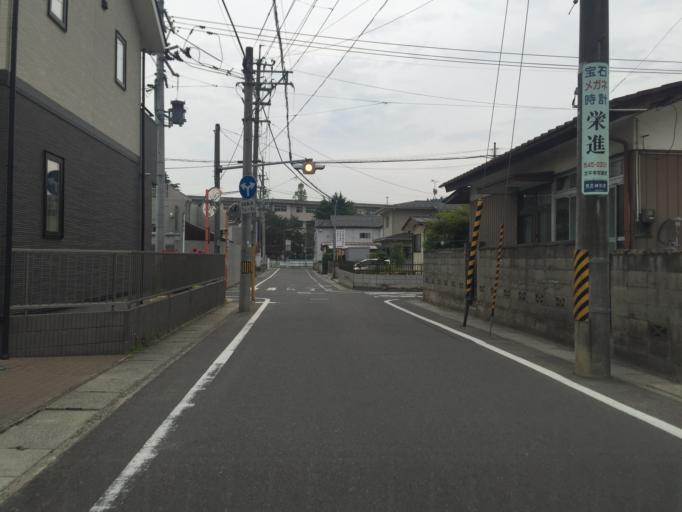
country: JP
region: Fukushima
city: Fukushima-shi
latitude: 37.7256
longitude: 140.4638
